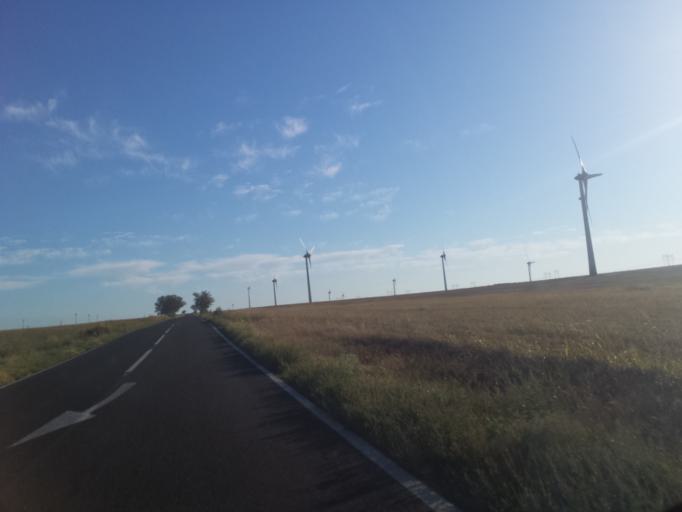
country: RO
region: Constanta
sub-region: Comuna Saraiu
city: Saraiu
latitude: 44.7760
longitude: 28.2244
